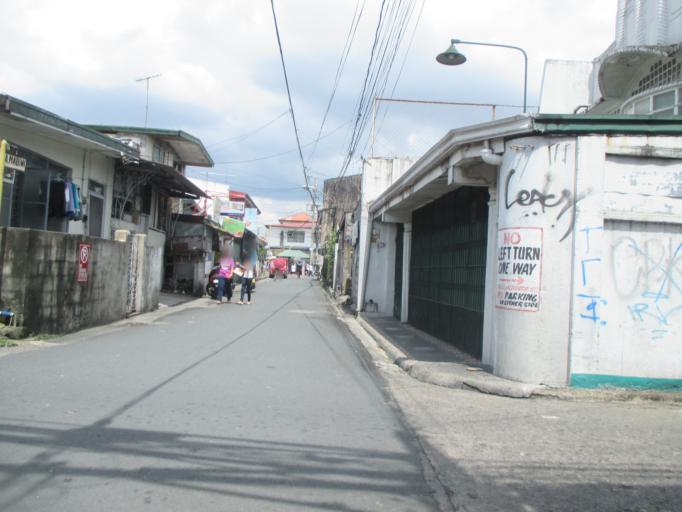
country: PH
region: Metro Manila
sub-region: Marikina
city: Calumpang
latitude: 14.6294
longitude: 121.0970
